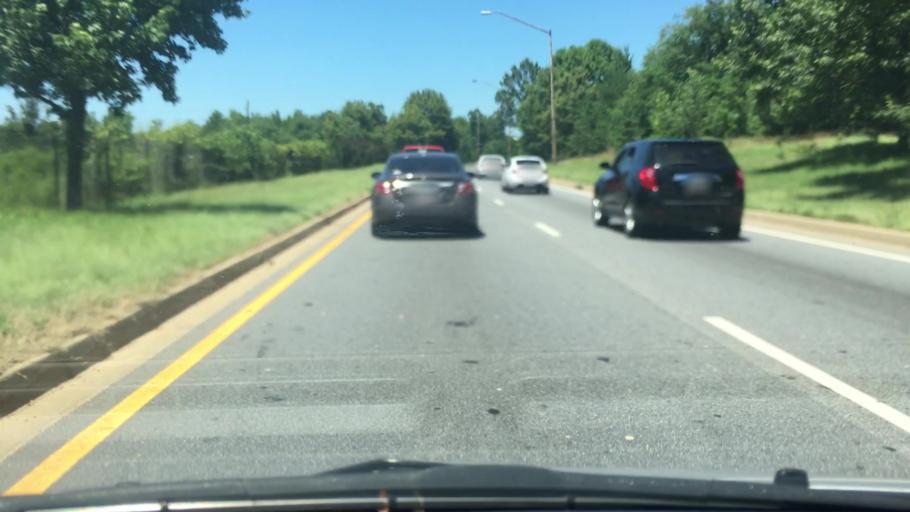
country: US
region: Maryland
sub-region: Prince George's County
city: Brandywine
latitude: 38.6559
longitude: -76.8745
